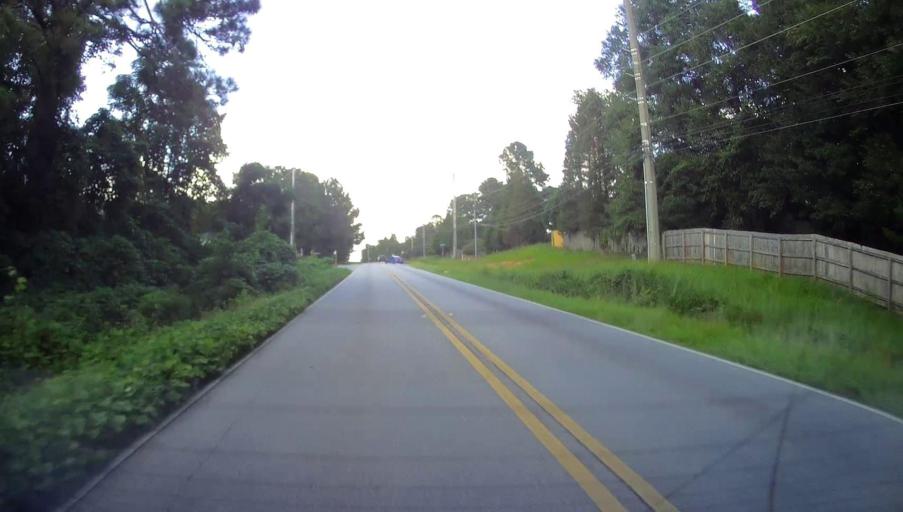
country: US
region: Georgia
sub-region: Muscogee County
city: Columbus
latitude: 32.5406
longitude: -84.8977
